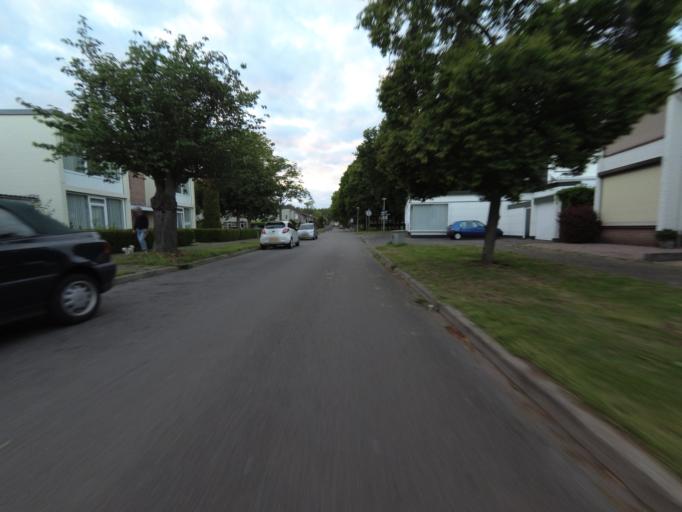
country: NL
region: Limburg
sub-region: Gemeente Maastricht
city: Heer
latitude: 50.8634
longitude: 5.7293
